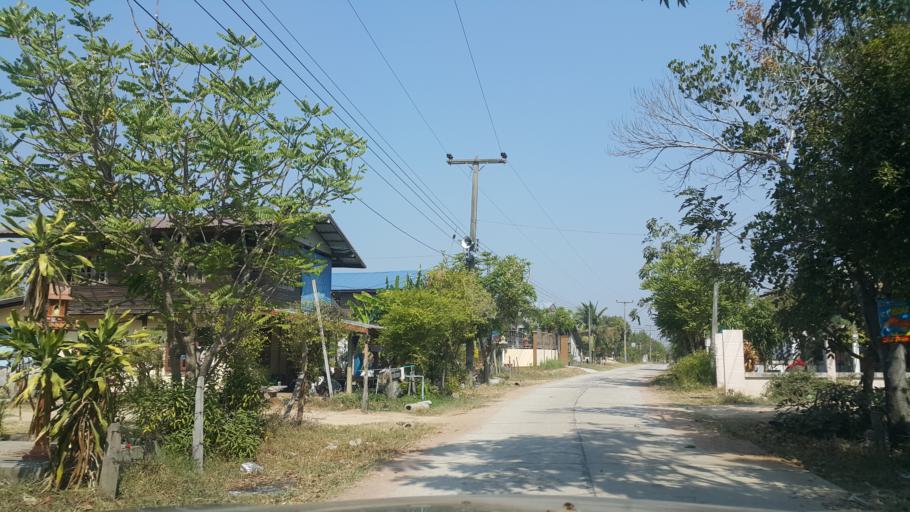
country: TH
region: Buriram
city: Krasang
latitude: 15.1085
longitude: 103.3790
